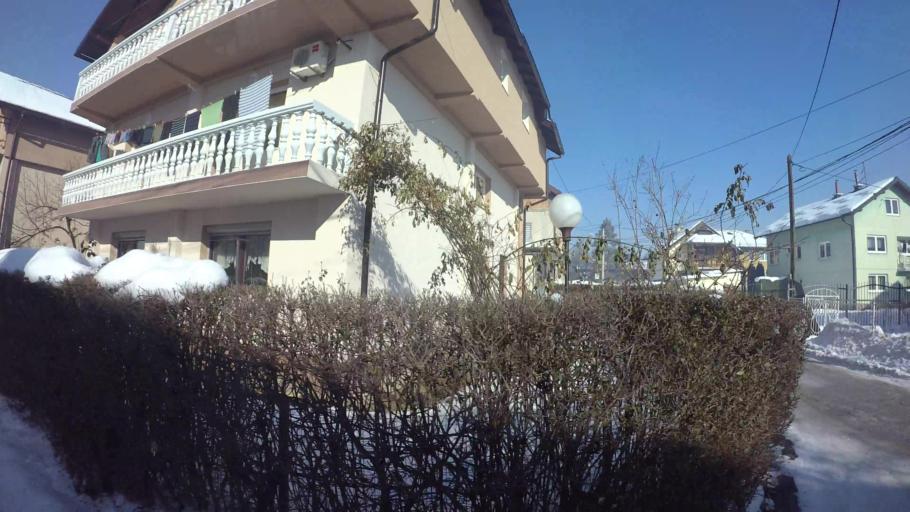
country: BA
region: Federation of Bosnia and Herzegovina
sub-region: Kanton Sarajevo
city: Sarajevo
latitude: 43.7957
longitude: 18.3131
